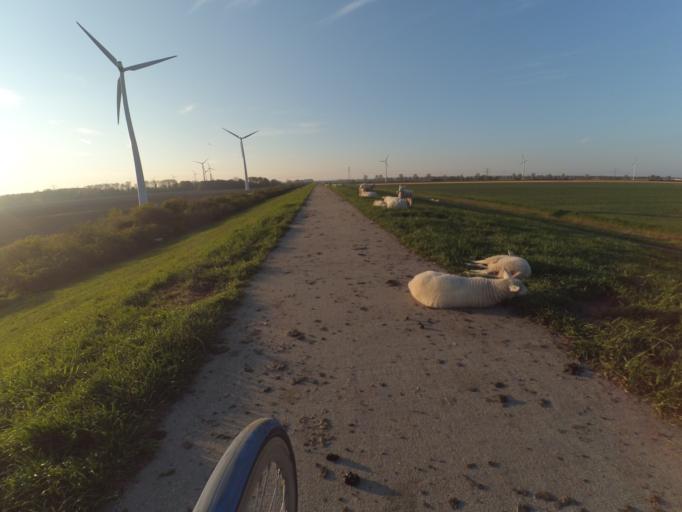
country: NL
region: Flevoland
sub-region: Gemeente Zeewolde
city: Zeewolde
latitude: 52.3885
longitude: 5.5266
